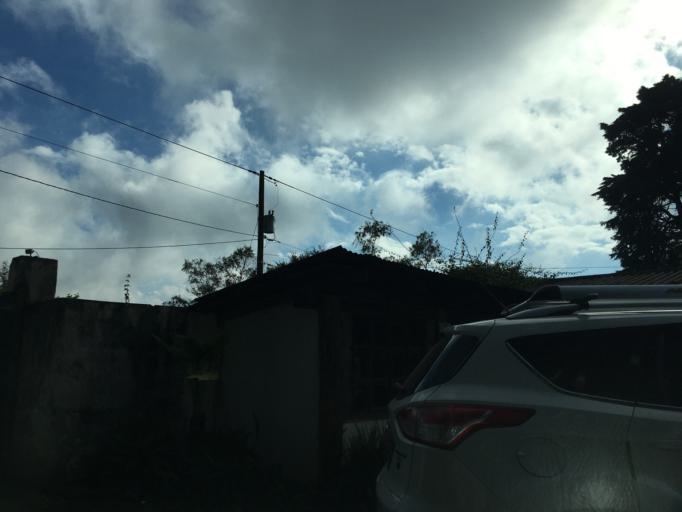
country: GT
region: Guatemala
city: San Jose Pinula
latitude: 14.6060
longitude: -90.4307
